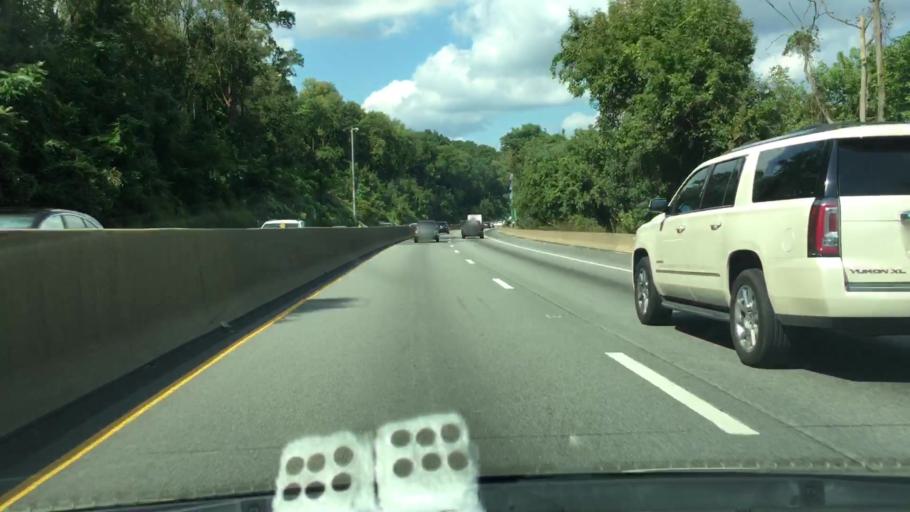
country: US
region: Pennsylvania
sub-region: Montgomery County
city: Conshohocken
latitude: 40.0626
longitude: -75.2754
